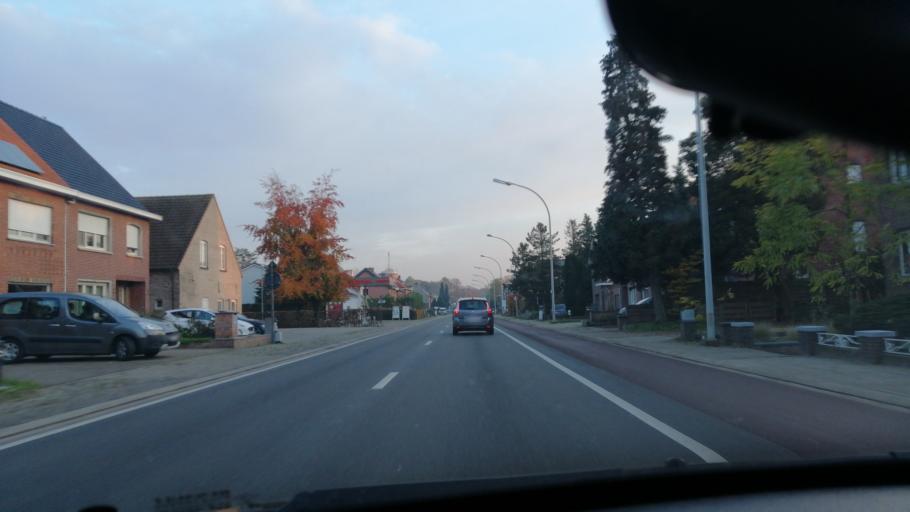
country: BE
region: Flanders
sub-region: Provincie Antwerpen
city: Herentals
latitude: 51.1916
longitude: 4.8307
